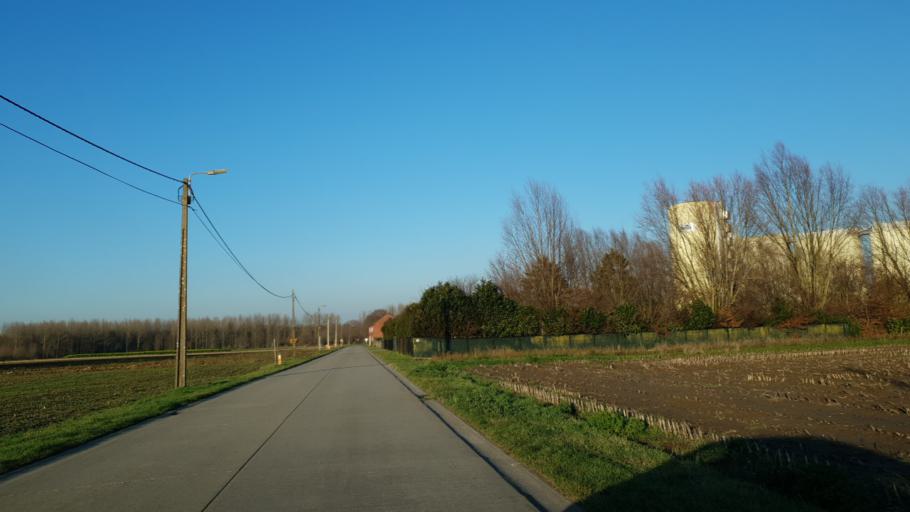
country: BE
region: Flanders
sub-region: Provincie Vlaams-Brabant
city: Herent
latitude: 50.9262
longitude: 4.6767
